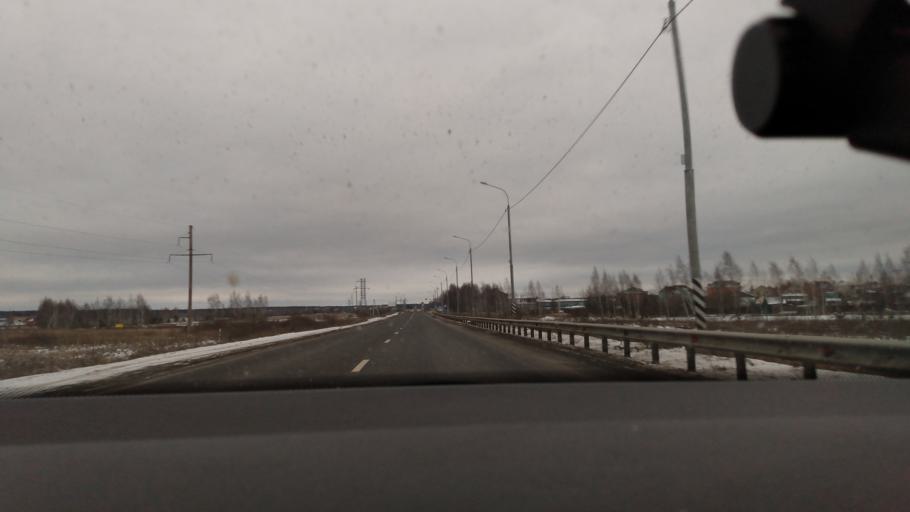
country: RU
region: Moskovskaya
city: Yegor'yevsk
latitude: 55.3952
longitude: 39.0680
